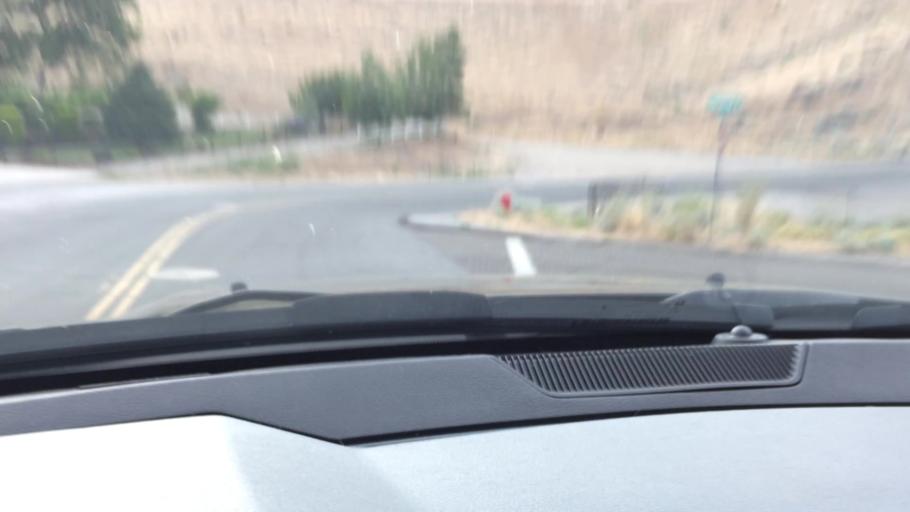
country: US
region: Nevada
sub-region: Washoe County
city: Reno
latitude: 39.4973
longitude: -119.8374
